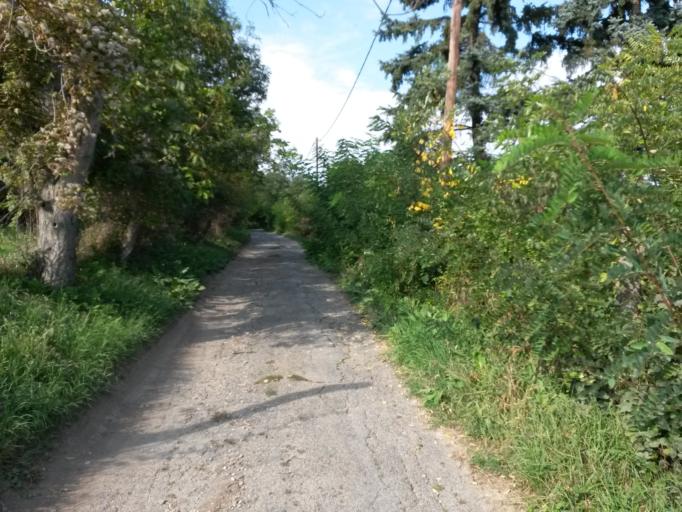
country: HU
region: Pest
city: Budaors
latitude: 47.4640
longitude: 18.9888
